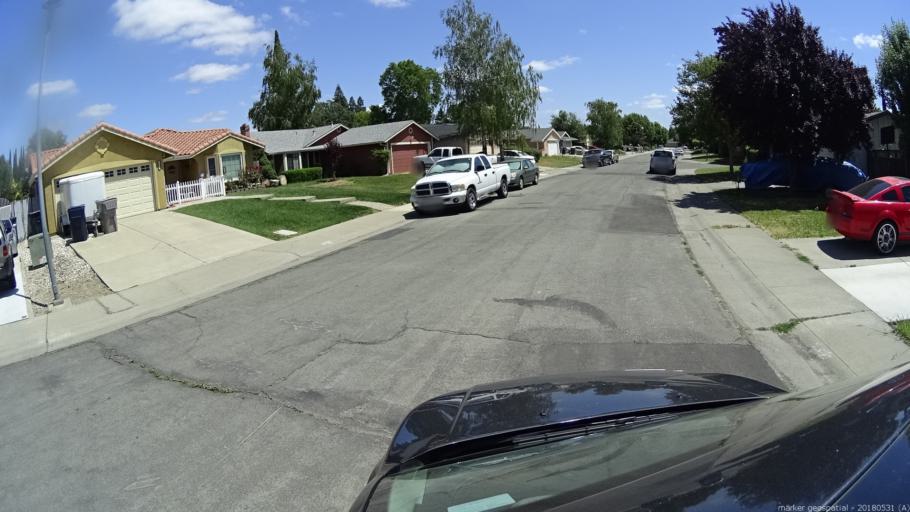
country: US
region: California
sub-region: Sacramento County
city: Sacramento
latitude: 38.6194
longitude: -121.5129
